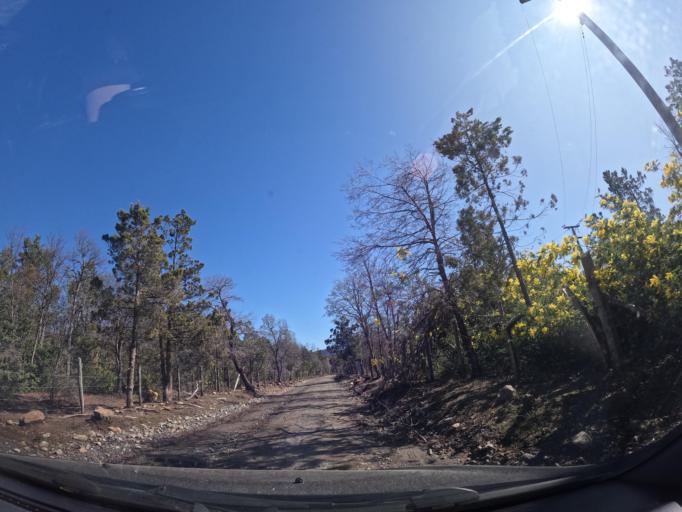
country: CL
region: Maule
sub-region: Provincia de Linares
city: Longavi
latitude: -36.2429
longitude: -71.3483
